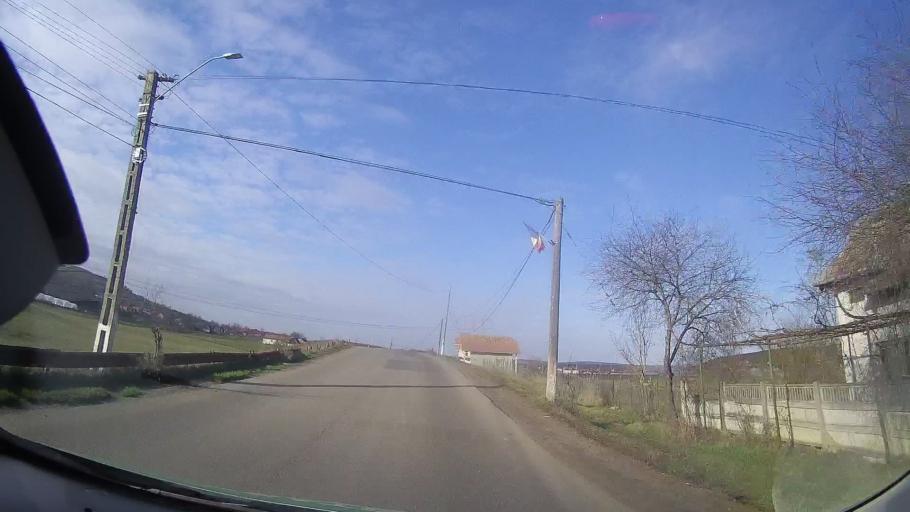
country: RO
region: Mures
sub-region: Comuna Valea Larga
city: Valea Larga
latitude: 46.6128
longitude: 24.0888
